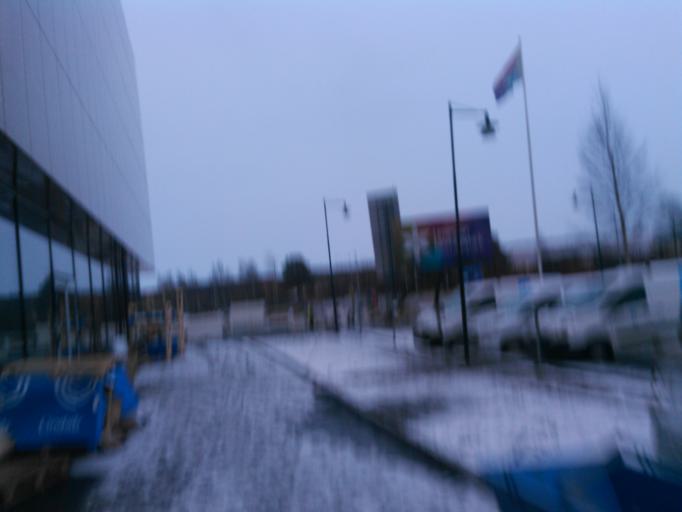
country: SE
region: Vaesterbotten
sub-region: Umea Kommun
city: Umea
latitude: 63.8347
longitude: 20.2651
